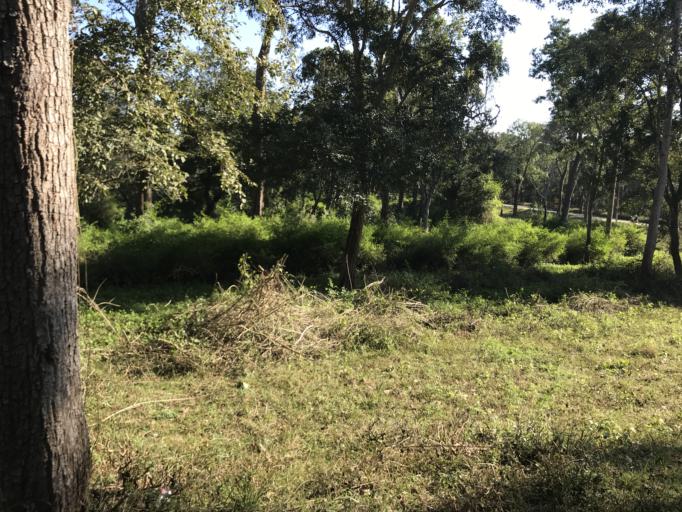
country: IN
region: Karnataka
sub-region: Mysore
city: Heggadadevankote
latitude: 11.9540
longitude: 76.2284
